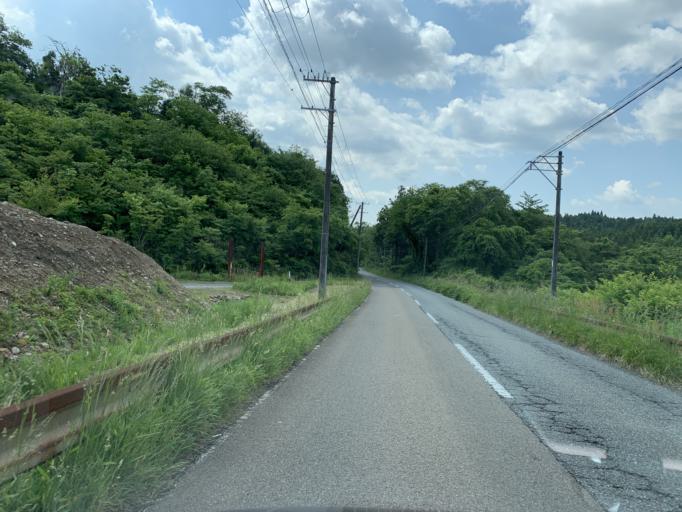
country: JP
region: Miyagi
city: Furukawa
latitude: 38.7755
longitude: 140.9603
